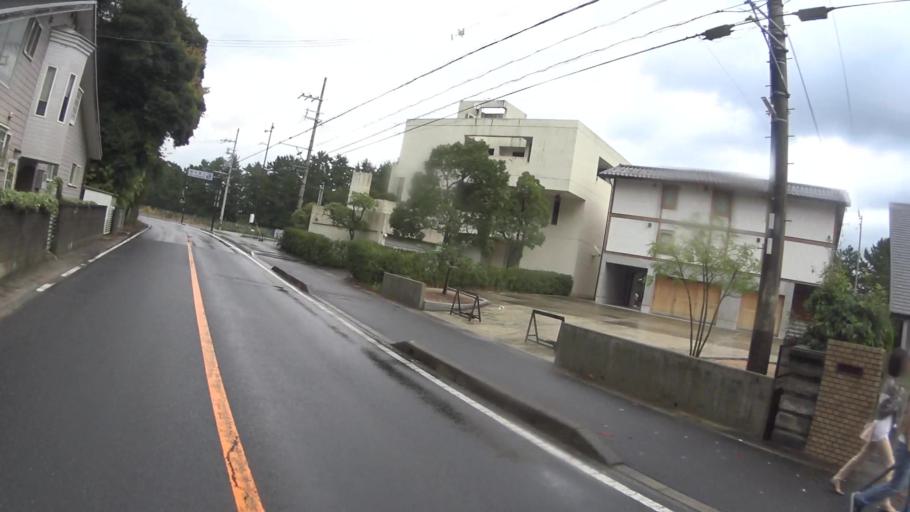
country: JP
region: Kyoto
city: Miyazu
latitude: 35.5535
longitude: 135.1856
